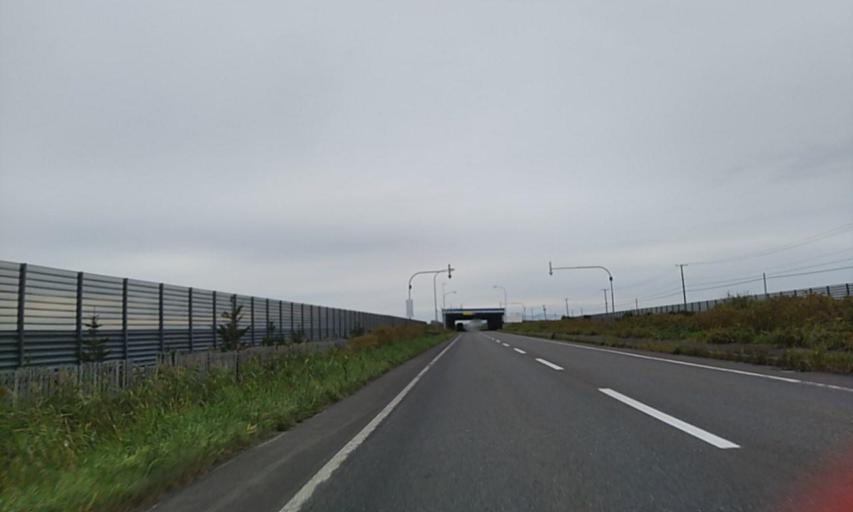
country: JP
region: Hokkaido
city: Makubetsu
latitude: 45.2976
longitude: 142.2079
